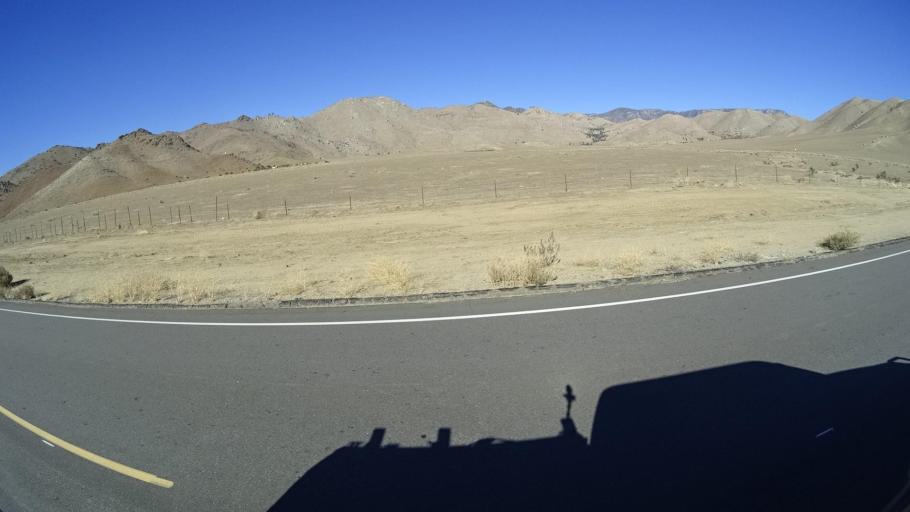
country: US
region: California
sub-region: Kern County
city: Weldon
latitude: 35.6785
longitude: -118.3672
